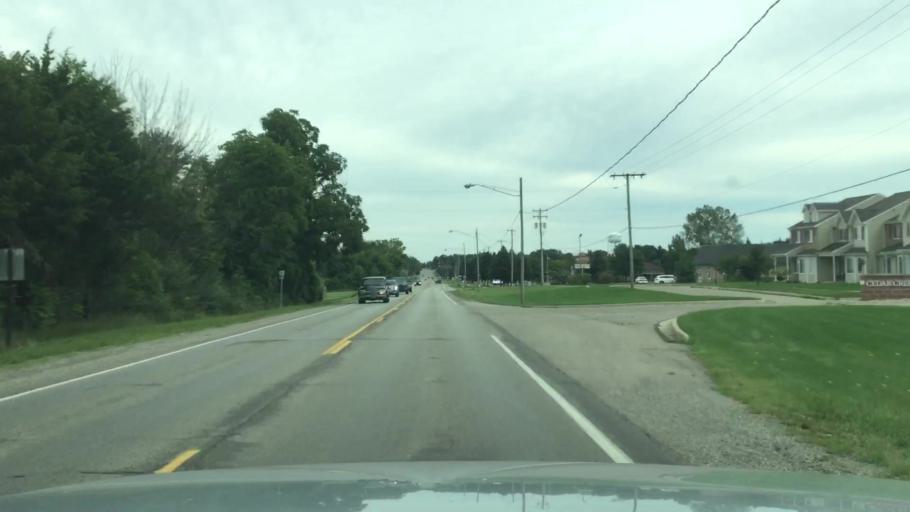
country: US
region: Michigan
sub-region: Genesee County
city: Swartz Creek
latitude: 42.9570
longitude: -83.8610
